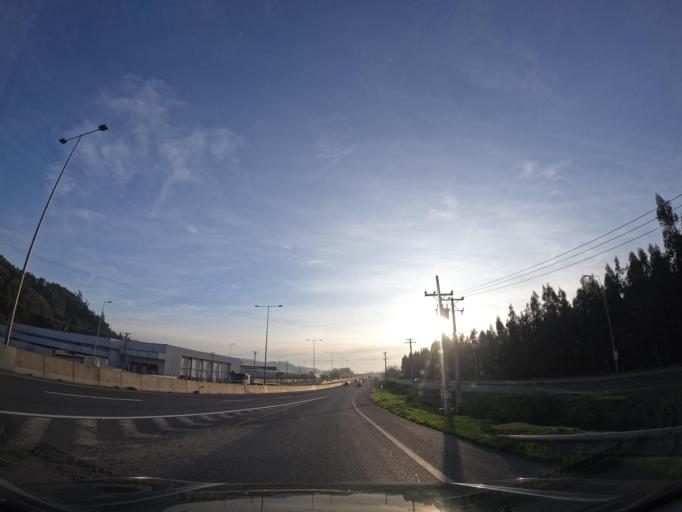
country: CL
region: Biobio
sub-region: Provincia de Concepcion
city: Concepcion
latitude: -36.8207
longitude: -72.9980
